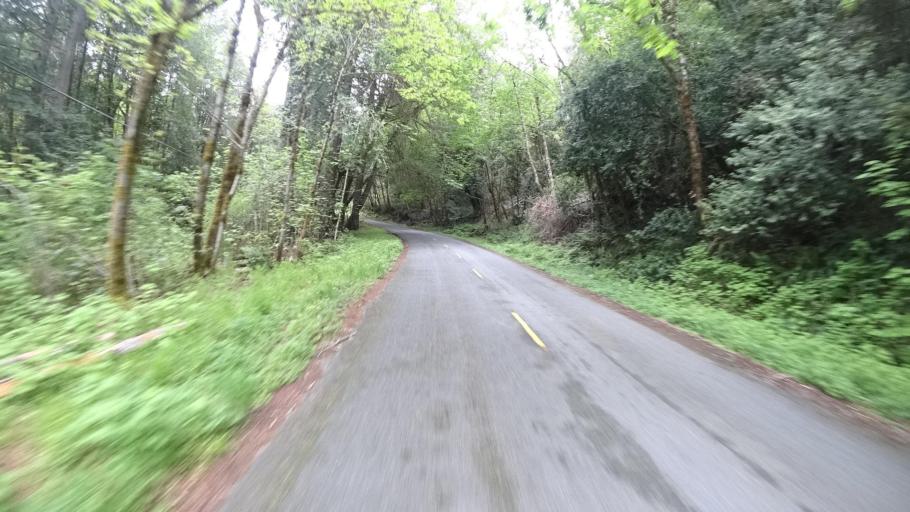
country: US
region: California
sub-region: Humboldt County
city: Blue Lake
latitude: 40.9588
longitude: -123.8380
